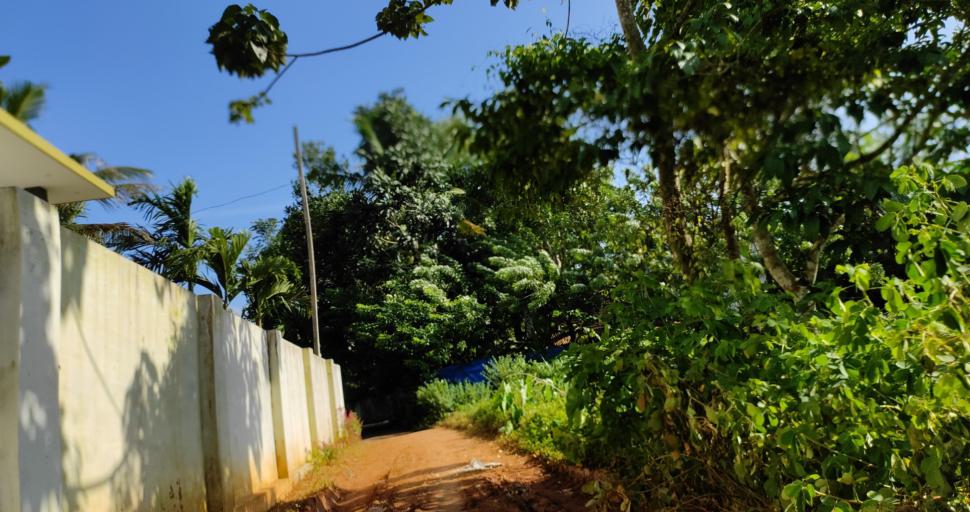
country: IN
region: Kerala
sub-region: Alappuzha
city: Shertallai
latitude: 9.6099
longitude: 76.3347
